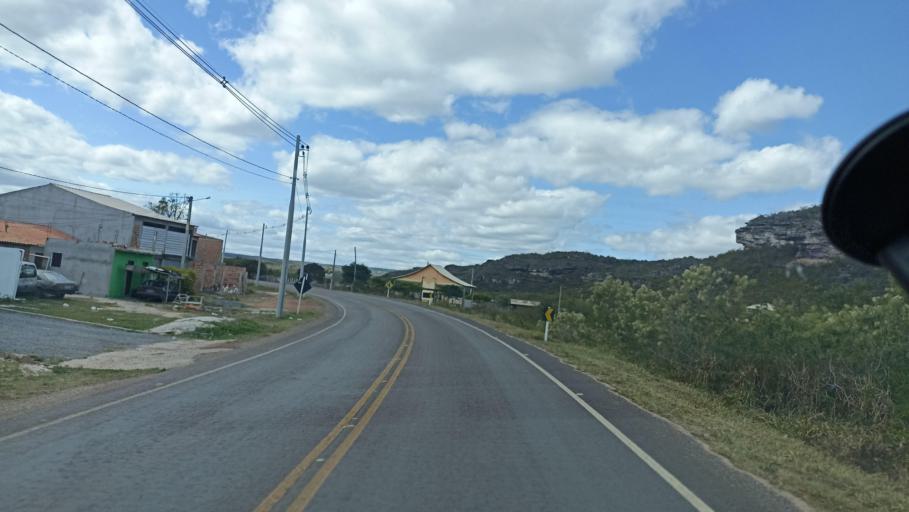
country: BR
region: Bahia
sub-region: Andarai
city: Vera Cruz
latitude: -13.0126
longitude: -41.3700
